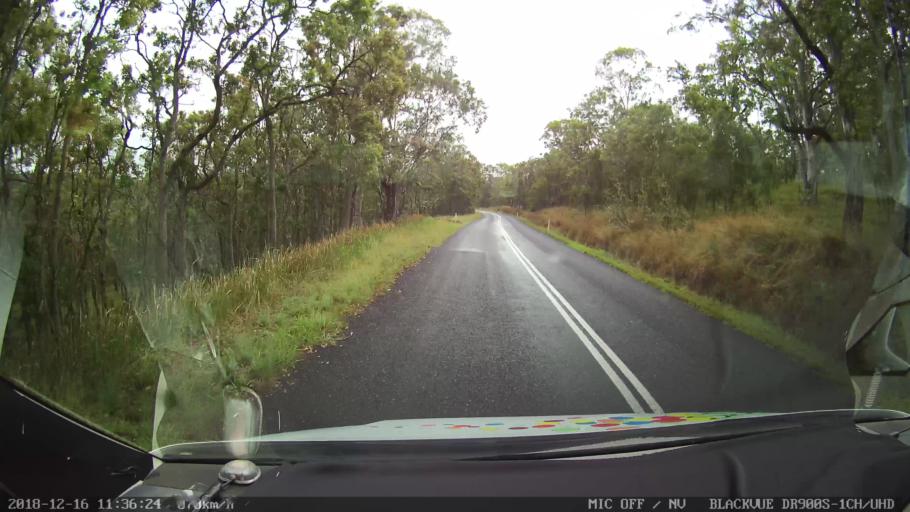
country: AU
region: New South Wales
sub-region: Tenterfield Municipality
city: Carrolls Creek
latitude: -28.9813
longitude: 152.1698
